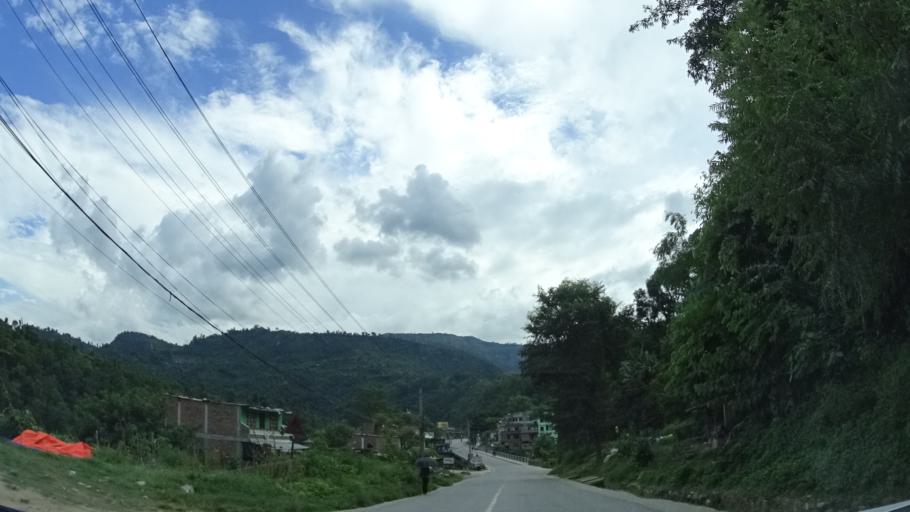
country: NP
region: Central Region
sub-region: Narayani Zone
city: Bharatpur
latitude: 27.8085
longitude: 84.8346
